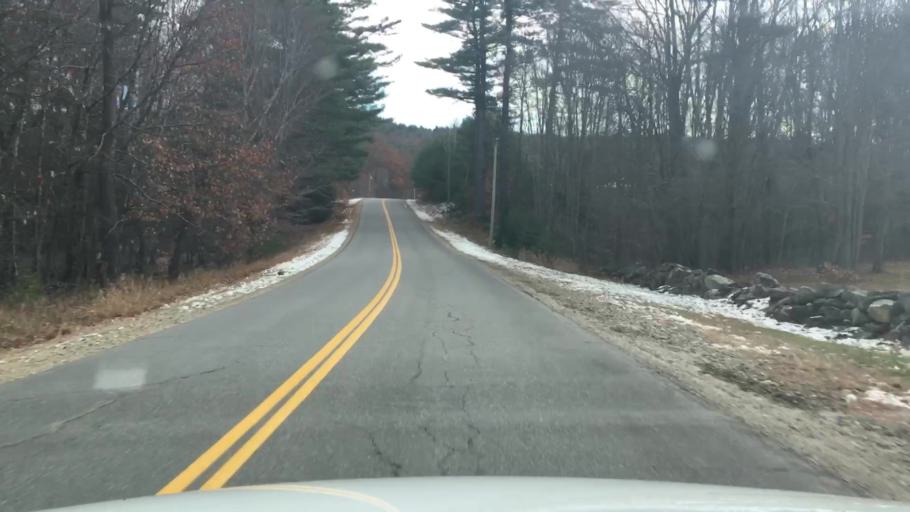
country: US
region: Maine
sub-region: Oxford County
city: Canton
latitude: 44.4902
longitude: -70.3261
